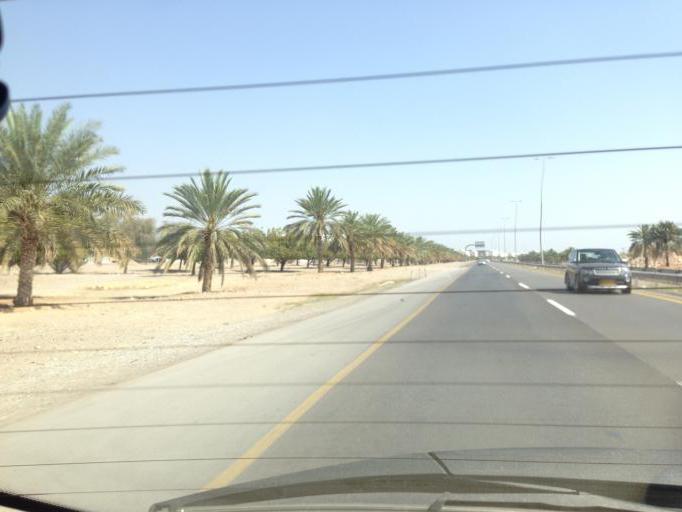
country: OM
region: Muhafazat Masqat
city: As Sib al Jadidah
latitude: 23.5810
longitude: 58.1957
